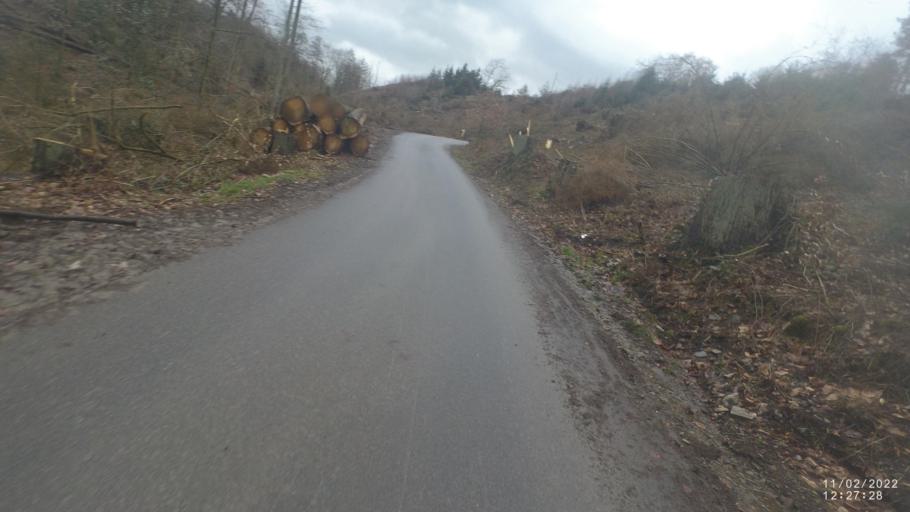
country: DE
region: North Rhine-Westphalia
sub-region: Regierungsbezirk Arnsberg
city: Nachrodt-Wiblingwerde
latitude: 51.3151
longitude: 7.6319
